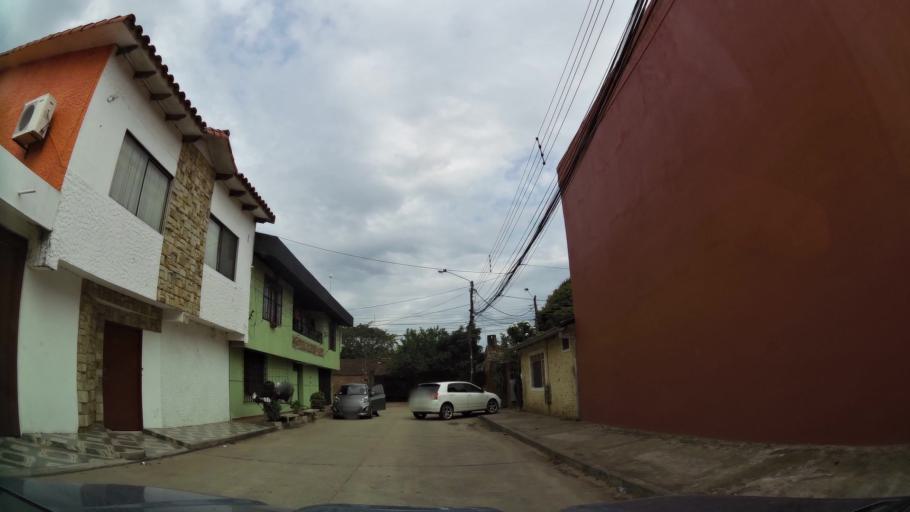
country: BO
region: Santa Cruz
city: Santa Cruz de la Sierra
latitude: -17.7750
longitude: -63.2080
